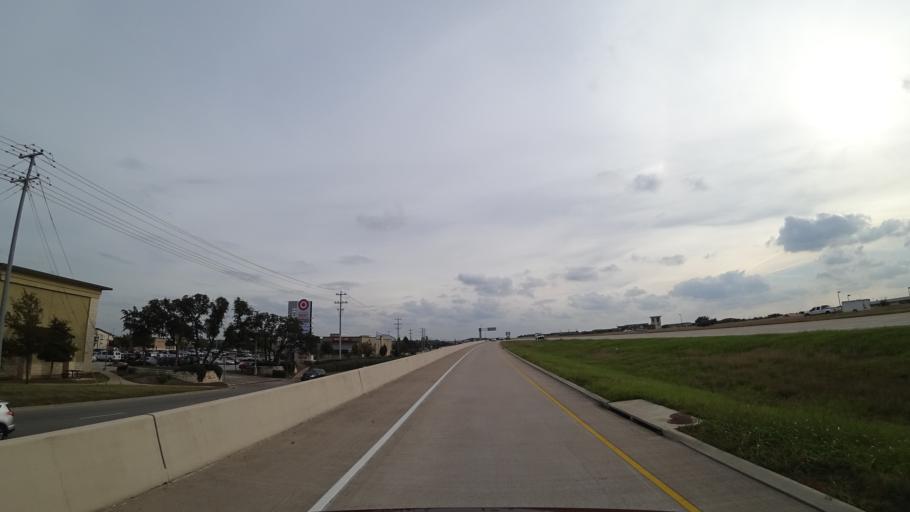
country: US
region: Texas
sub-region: Williamson County
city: Cedar Park
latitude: 30.5276
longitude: -97.8163
